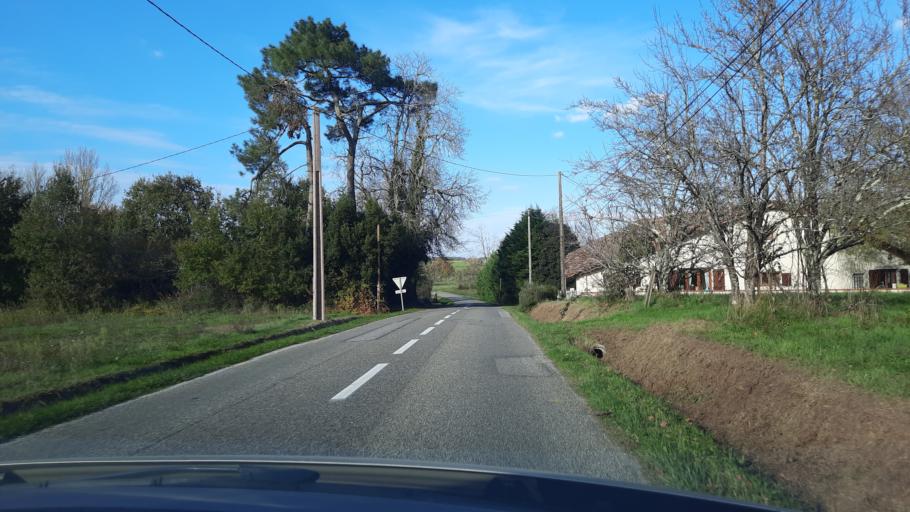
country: FR
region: Midi-Pyrenees
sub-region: Departement du Tarn-et-Garonne
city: Lafrancaise
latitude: 44.1569
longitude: 1.2658
